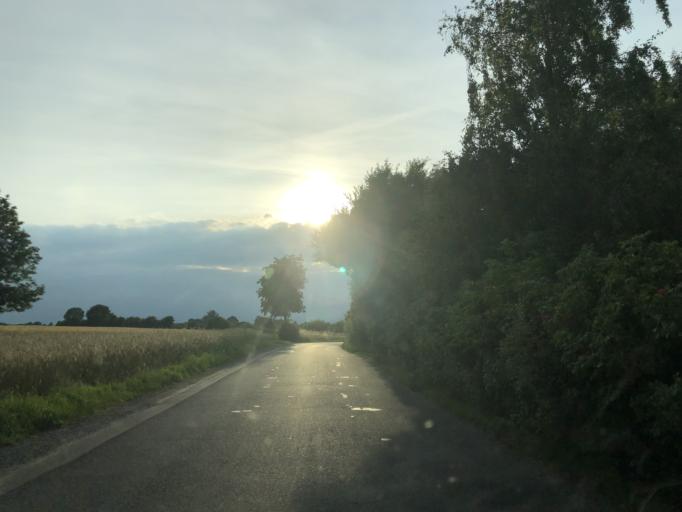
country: DK
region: South Denmark
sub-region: Vejle Kommune
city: Borkop
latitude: 55.6170
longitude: 9.6046
